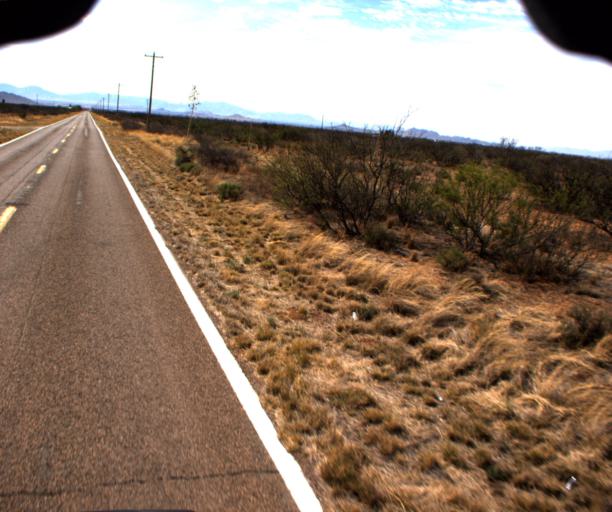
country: US
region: Arizona
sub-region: Cochise County
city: Willcox
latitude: 31.8761
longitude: -109.5586
